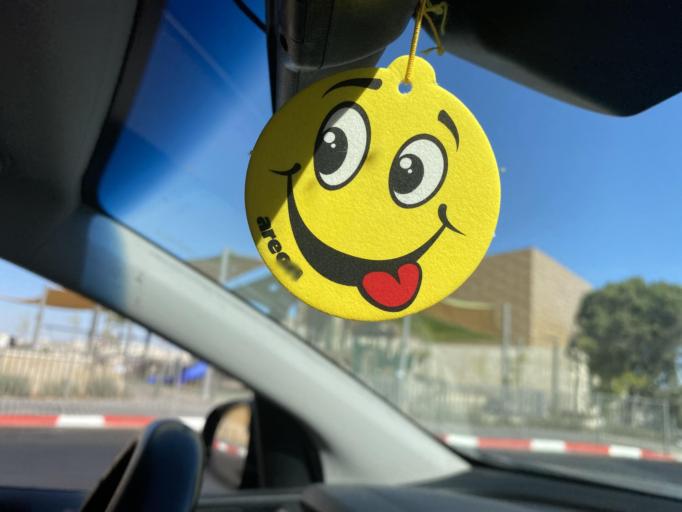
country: PS
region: West Bank
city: Bayt Iksa
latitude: 31.8171
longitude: 35.1941
